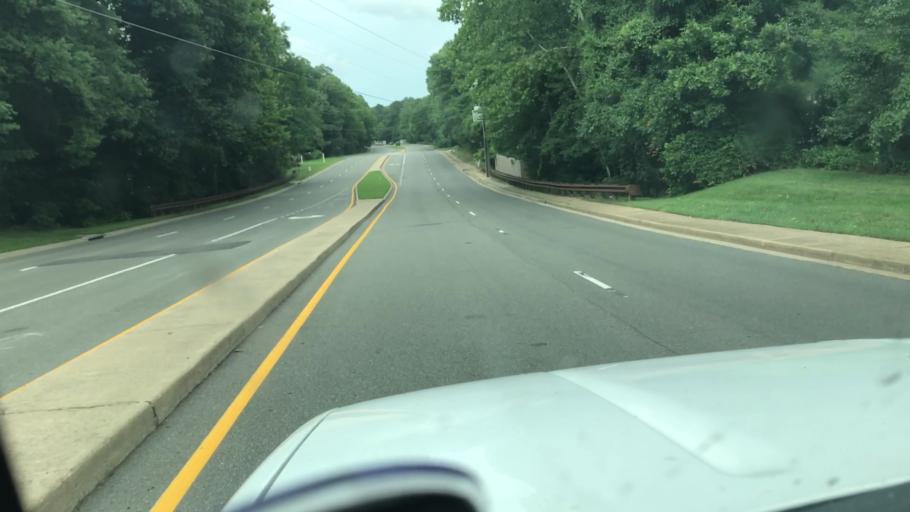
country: US
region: Virginia
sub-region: Henrico County
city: Tuckahoe
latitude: 37.6127
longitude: -77.5885
